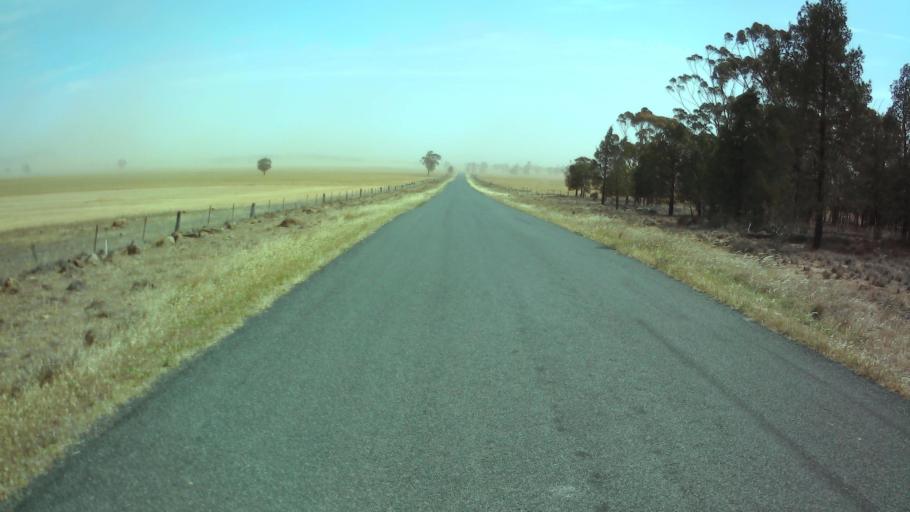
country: AU
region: New South Wales
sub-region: Weddin
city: Grenfell
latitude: -33.7457
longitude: 147.9917
